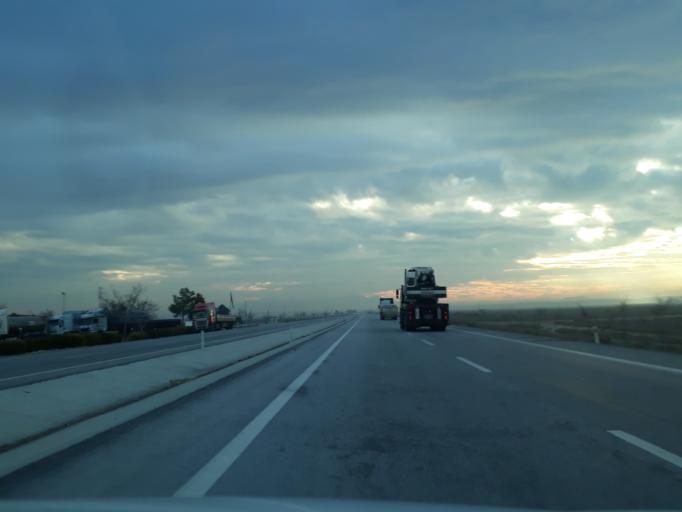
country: TR
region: Konya
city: Hotamis
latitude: 37.7126
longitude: 33.3843
